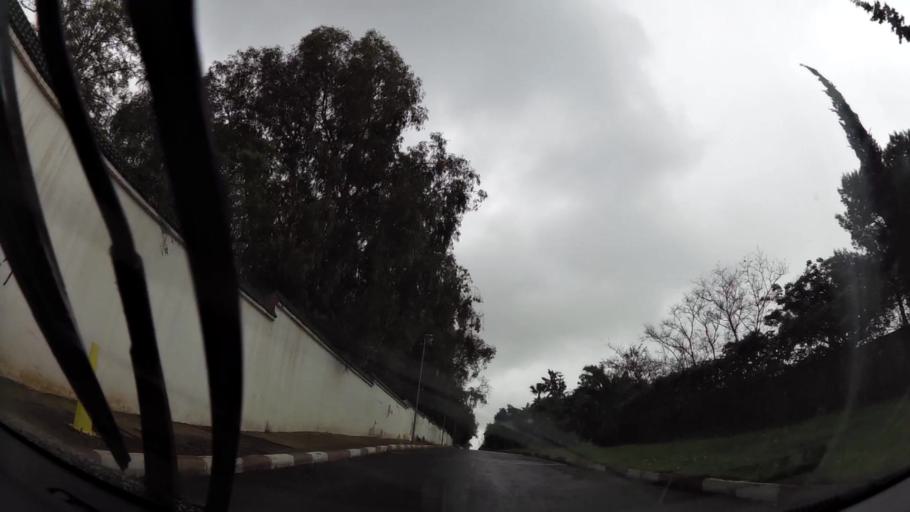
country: MA
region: Grand Casablanca
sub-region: Casablanca
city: Casablanca
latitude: 33.5277
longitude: -7.6307
